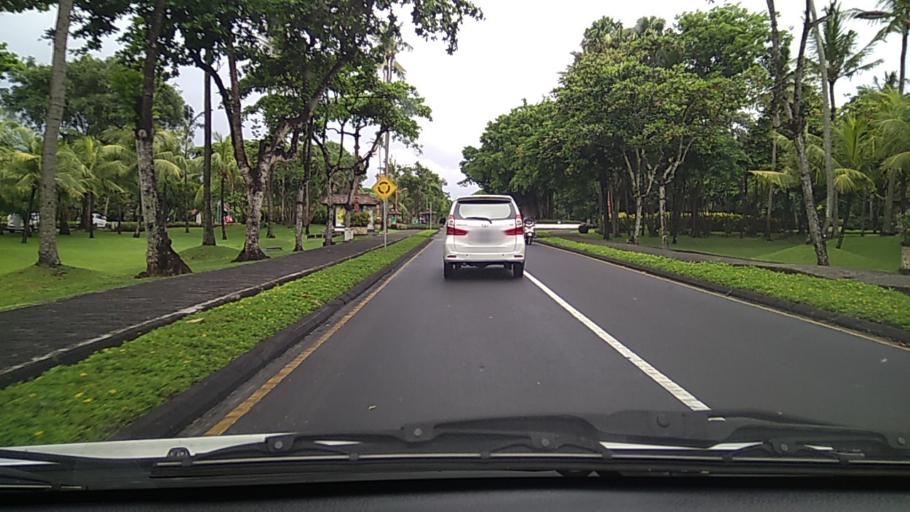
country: ID
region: Bali
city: Bualu
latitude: -8.8033
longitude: 115.2294
